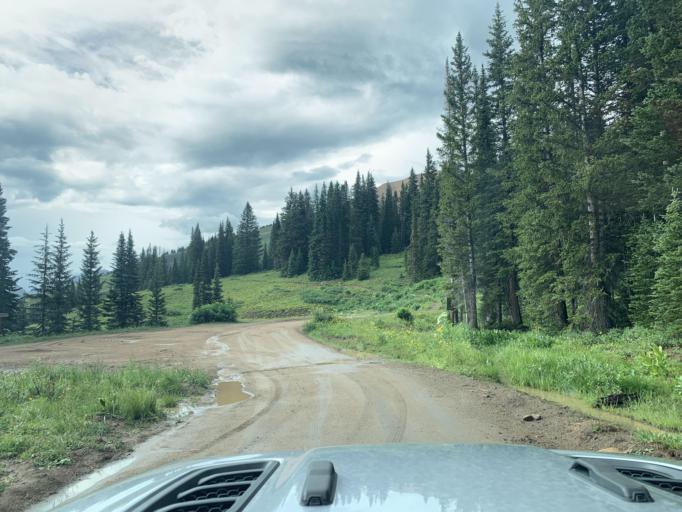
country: US
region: Colorado
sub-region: Gunnison County
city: Crested Butte
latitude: 38.9692
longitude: -107.0450
